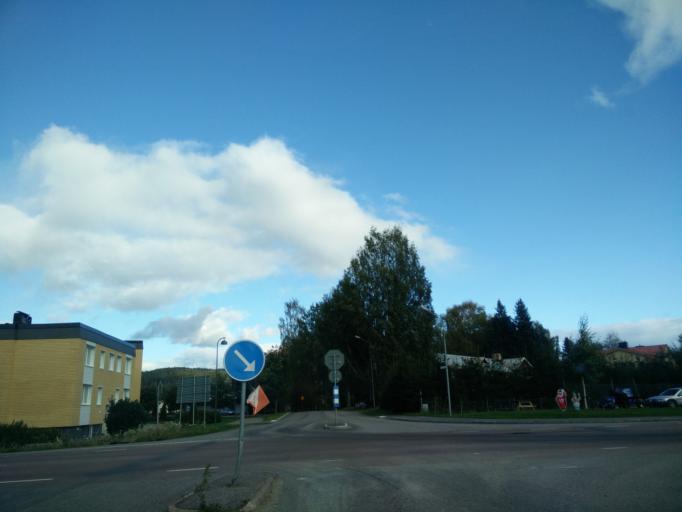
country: SE
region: Vaesternorrland
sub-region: Sundsvalls Kommun
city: Matfors
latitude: 62.3452
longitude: 17.0172
